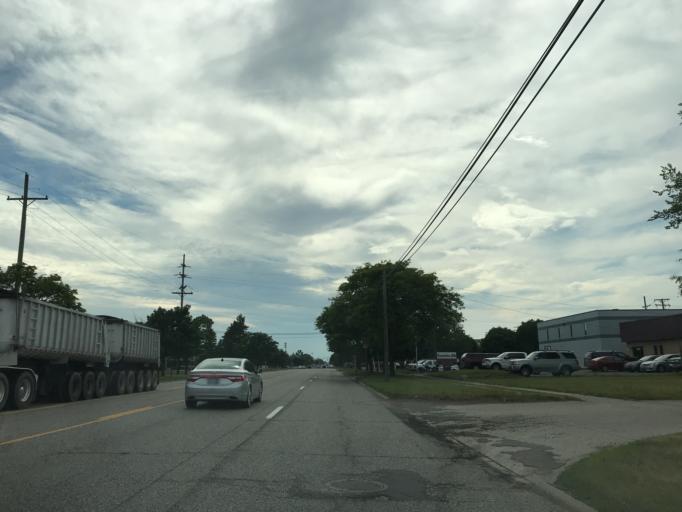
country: US
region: Michigan
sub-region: Oakland County
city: Farmington
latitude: 42.4413
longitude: -83.3508
